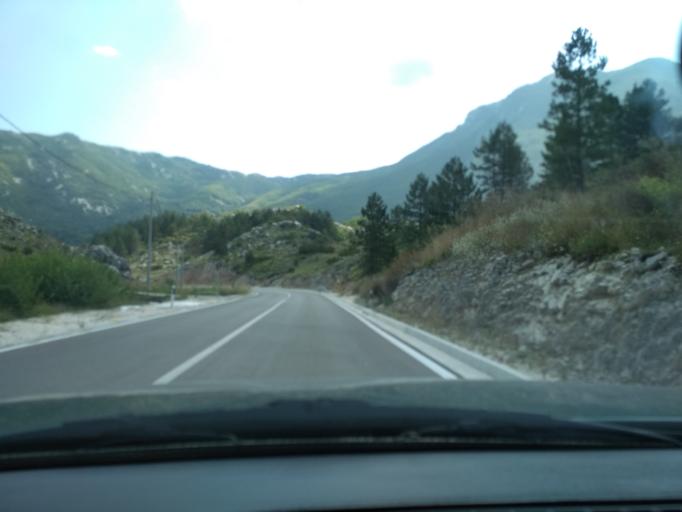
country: ME
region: Kotor
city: Kotor
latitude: 42.4282
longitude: 18.8163
